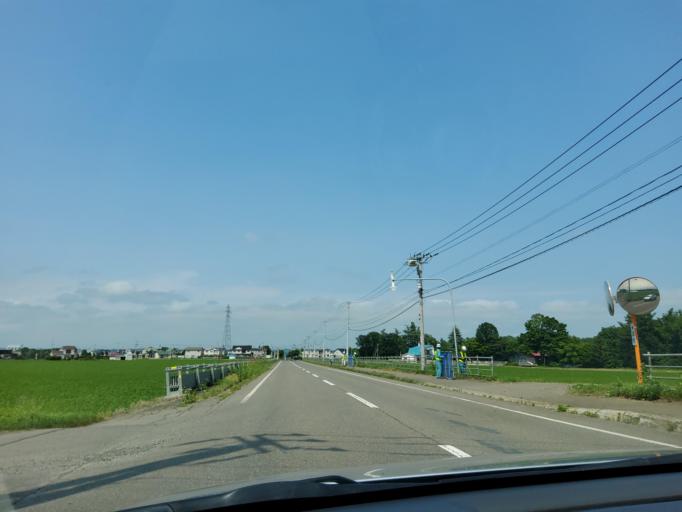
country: JP
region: Hokkaido
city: Obihiro
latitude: 42.8953
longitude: 143.0432
